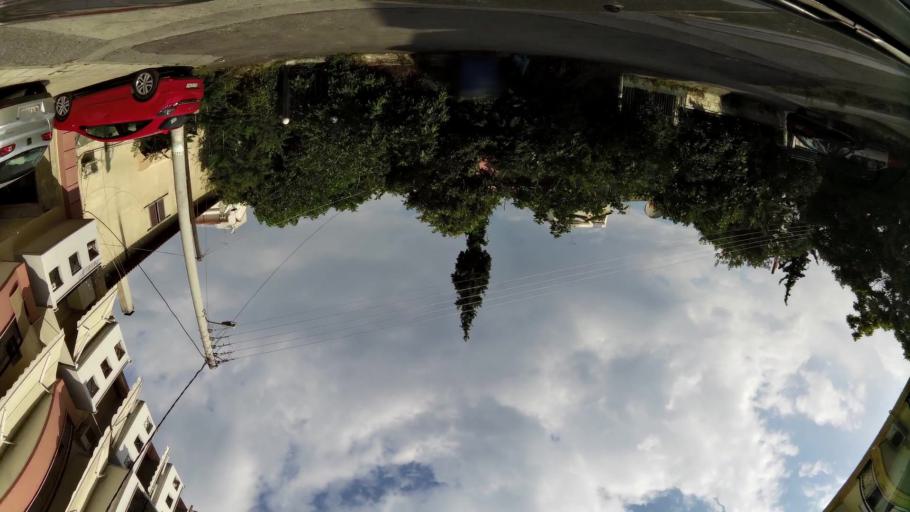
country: GR
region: Central Macedonia
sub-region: Nomos Thessalonikis
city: Sykies
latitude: 40.6586
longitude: 22.9603
